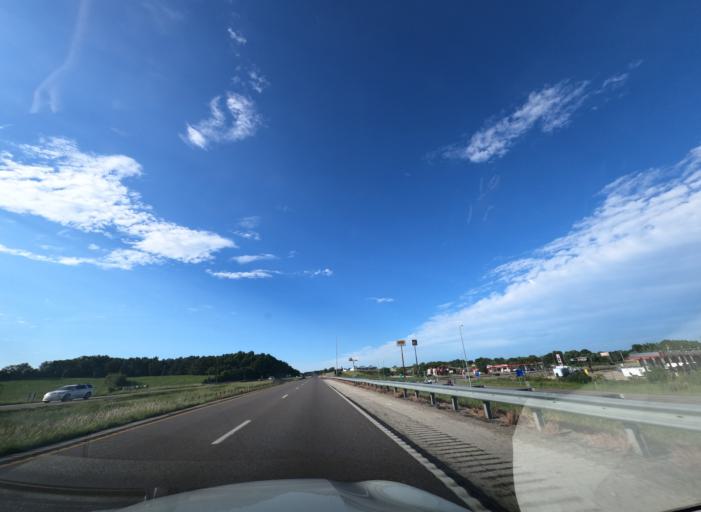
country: US
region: Missouri
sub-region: Jefferson County
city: Herculaneum
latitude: 38.2537
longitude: -90.4024
